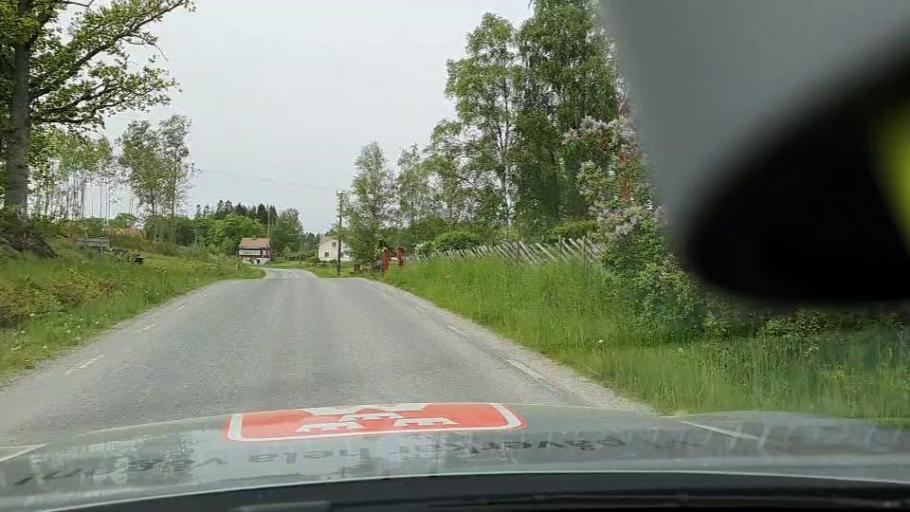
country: SE
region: Soedermanland
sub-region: Flens Kommun
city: Flen
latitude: 59.1023
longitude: 16.5518
